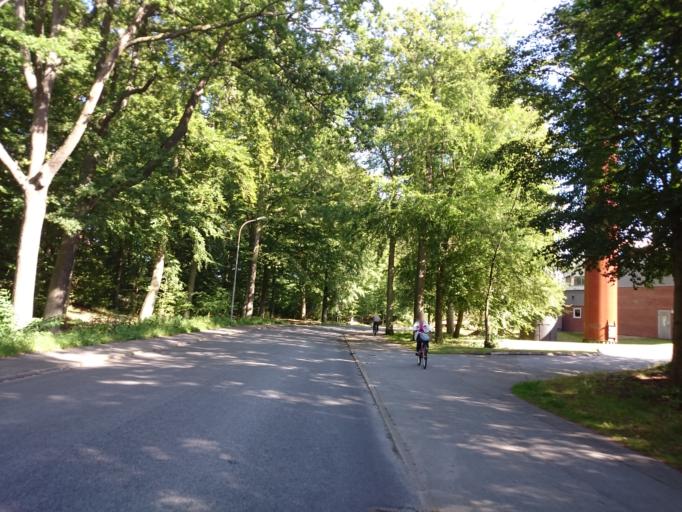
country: SE
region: Blekinge
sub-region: Karlshamns Kommun
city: Karlshamn
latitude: 56.1654
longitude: 14.8748
